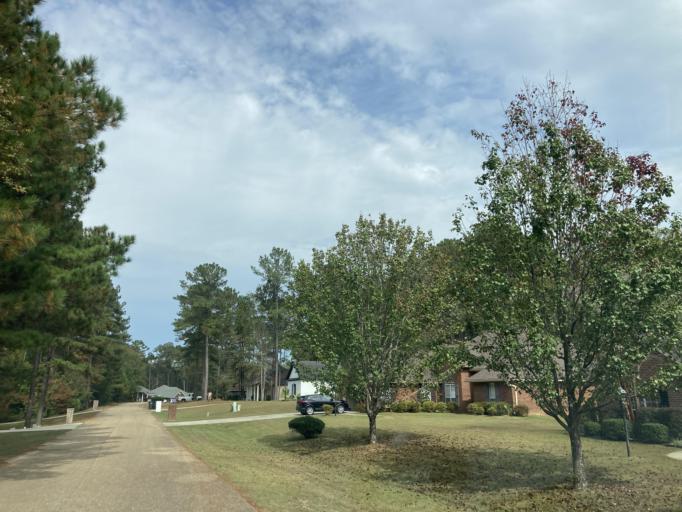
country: US
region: Mississippi
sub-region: Lamar County
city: Arnold Line
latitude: 31.3329
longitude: -89.4168
